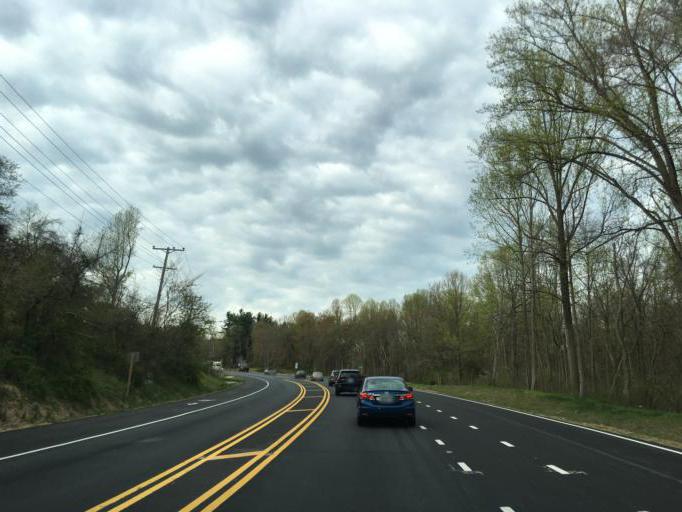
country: US
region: Maryland
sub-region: Carroll County
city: Sykesville
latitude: 39.3596
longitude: -76.9688
